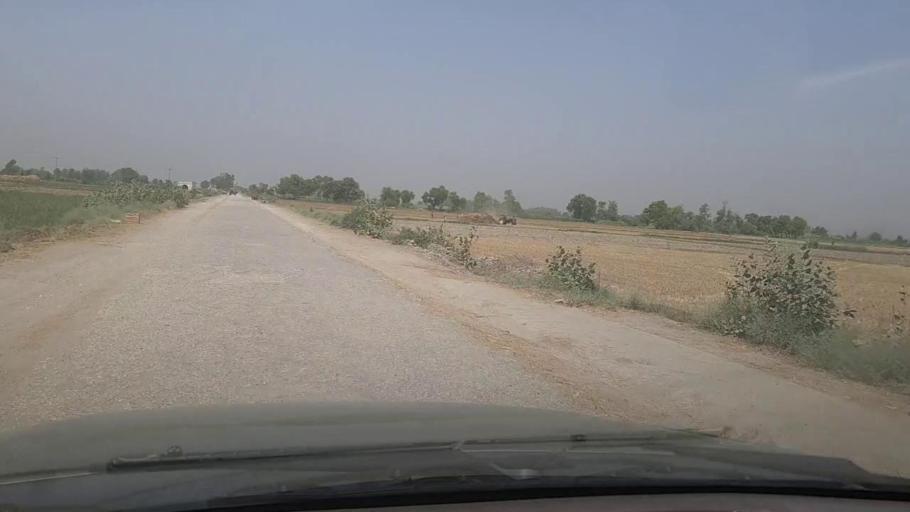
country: PK
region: Sindh
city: Madeji
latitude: 27.7959
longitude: 68.4684
